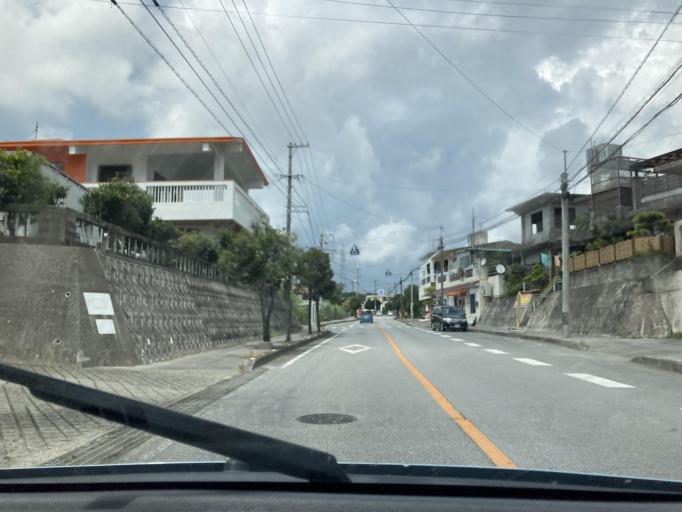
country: JP
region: Okinawa
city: Tomigusuku
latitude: 26.1642
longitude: 127.7558
